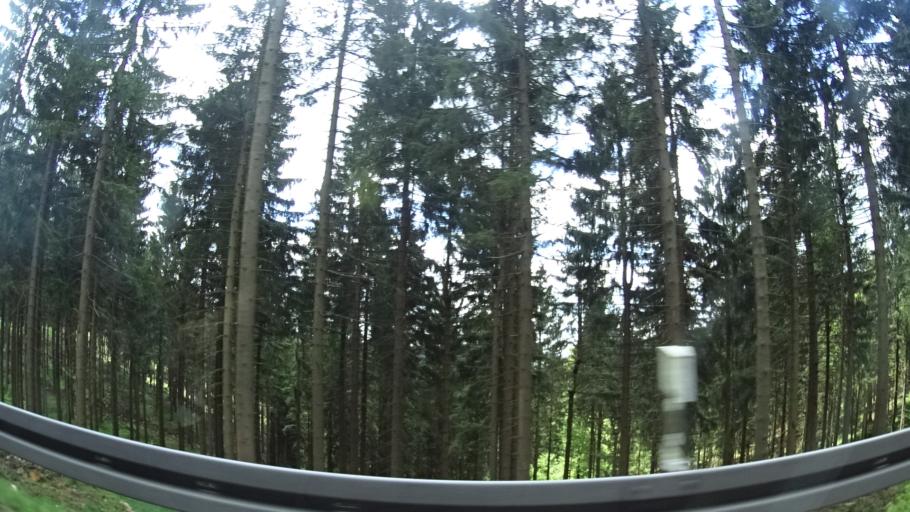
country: DE
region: Thuringia
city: Stutzerbach
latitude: 50.6033
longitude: 10.8955
